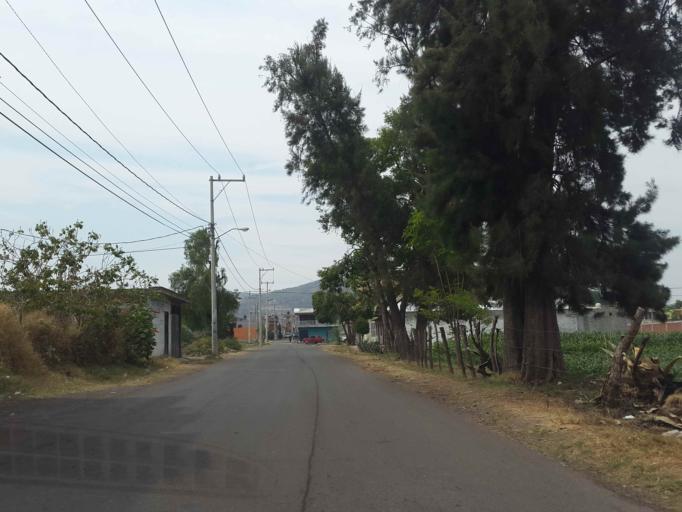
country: MX
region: Michoacan
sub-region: Tarimbaro
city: El Colegio
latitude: 19.7901
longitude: -101.1774
